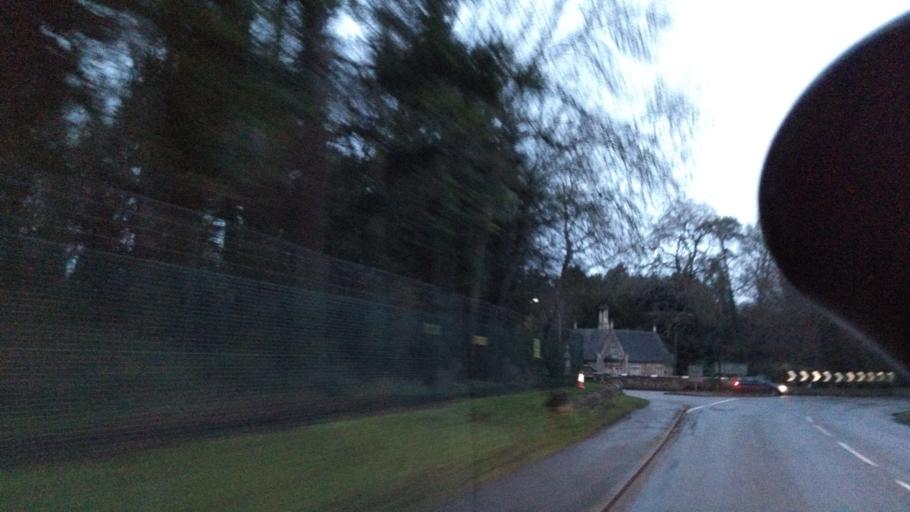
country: GB
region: England
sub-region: Oxfordshire
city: Shrivenham
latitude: 51.6056
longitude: -1.6453
